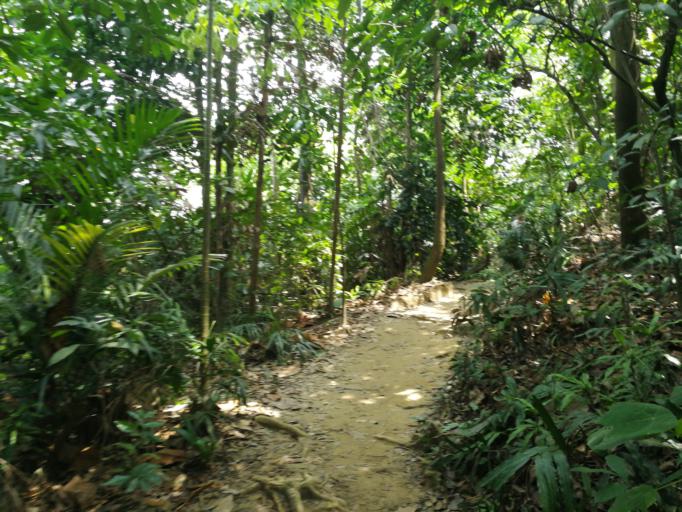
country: MY
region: Kuala Lumpur
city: Kuala Lumpur
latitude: 3.0996
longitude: 101.6583
